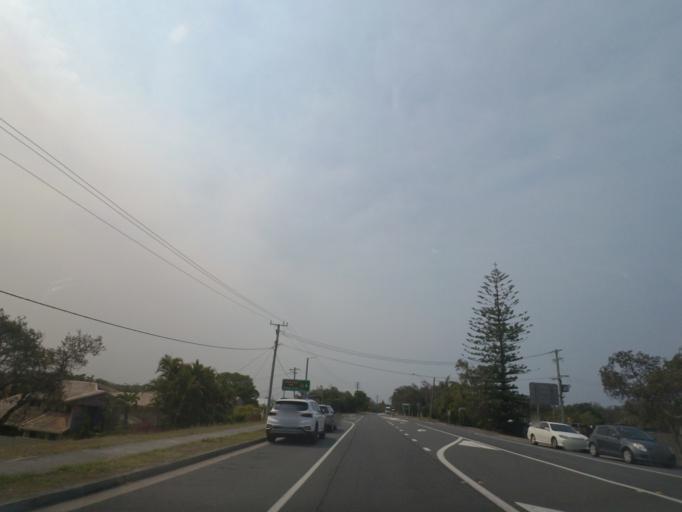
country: AU
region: New South Wales
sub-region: Tweed
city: Casuarina
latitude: -28.3296
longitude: 153.5688
